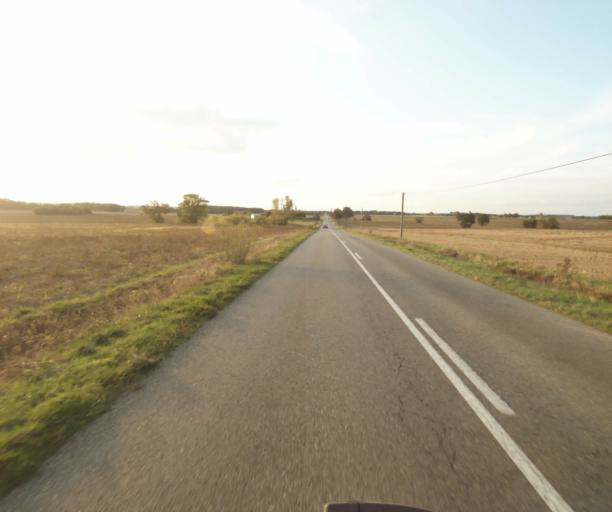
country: FR
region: Midi-Pyrenees
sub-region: Departement du Tarn-et-Garonne
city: Verdun-sur-Garonne
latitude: 43.8250
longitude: 1.1758
